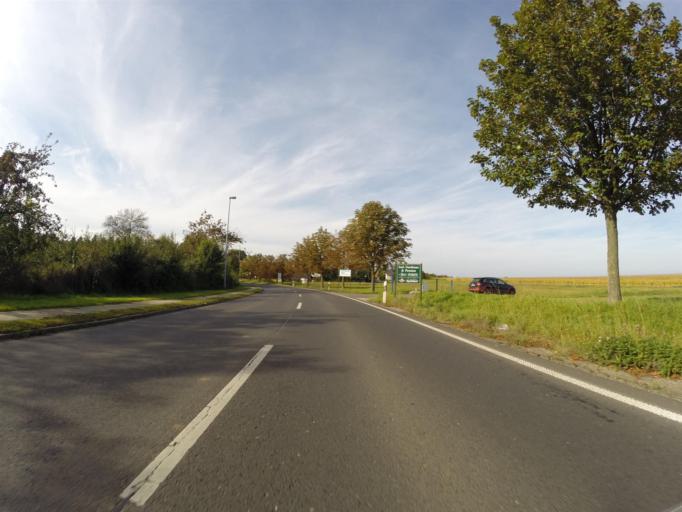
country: DE
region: Thuringia
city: Apolda
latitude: 50.9812
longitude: 11.5170
